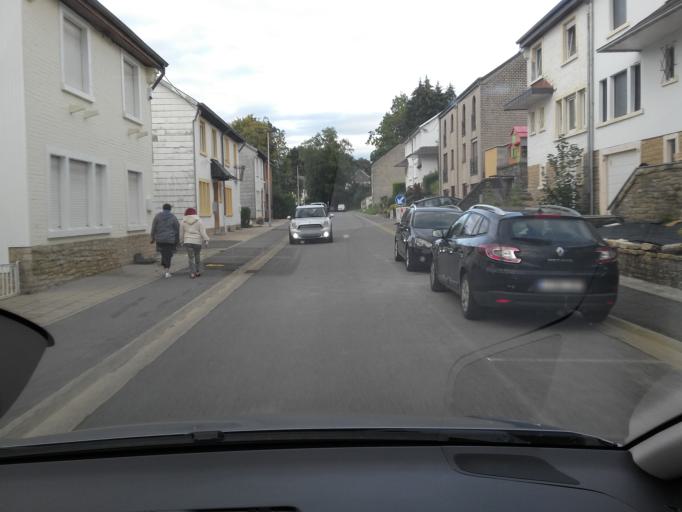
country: BE
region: Wallonia
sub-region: Province du Luxembourg
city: Arlon
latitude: 49.6878
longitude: 5.8010
